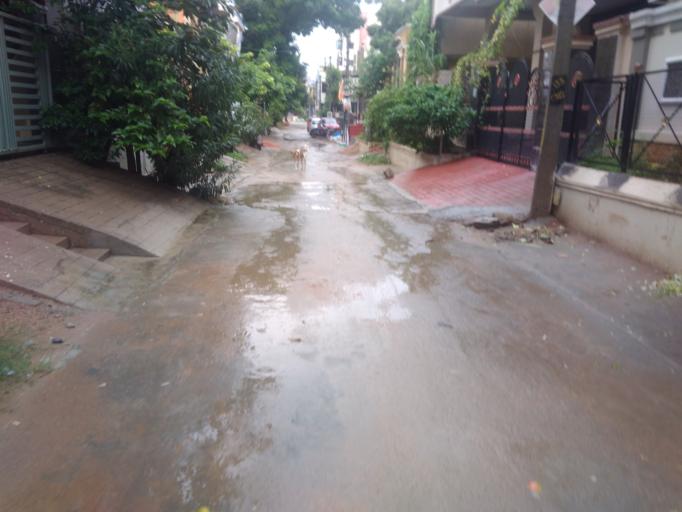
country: IN
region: Telangana
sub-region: Rangareddi
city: Secunderabad
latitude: 17.5141
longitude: 78.5093
